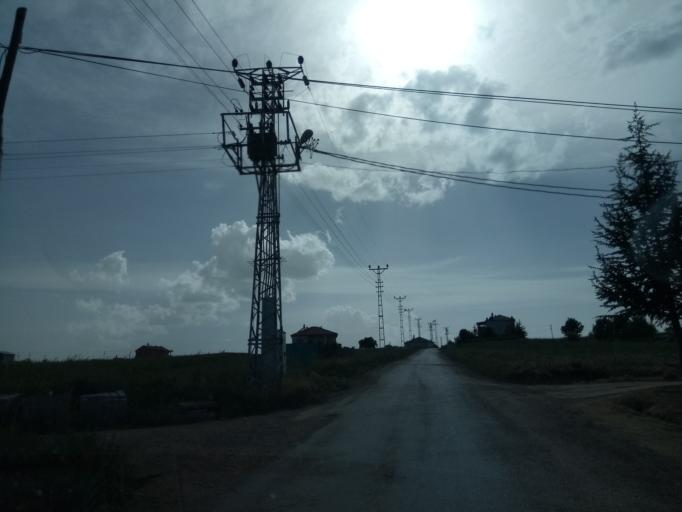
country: TR
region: Konya
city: Ahirli
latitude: 37.2842
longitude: 32.1811
